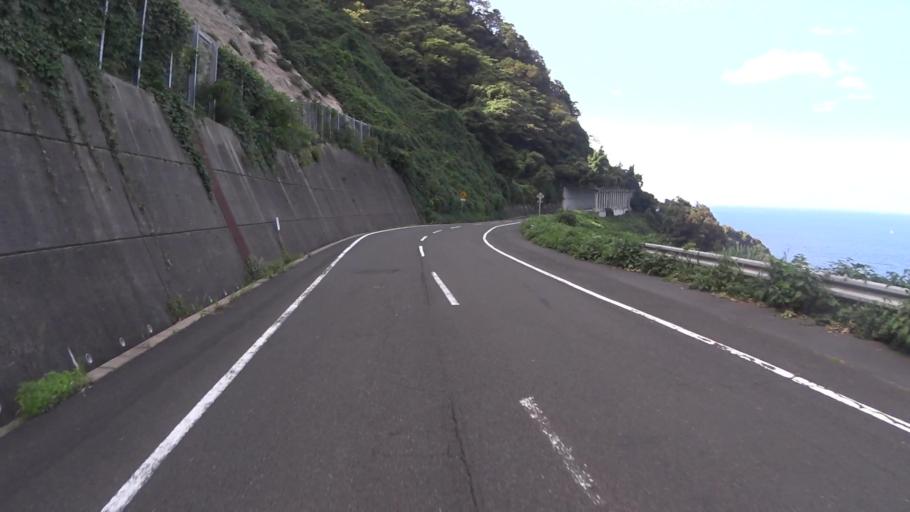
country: JP
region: Kyoto
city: Miyazu
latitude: 35.7607
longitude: 135.2407
